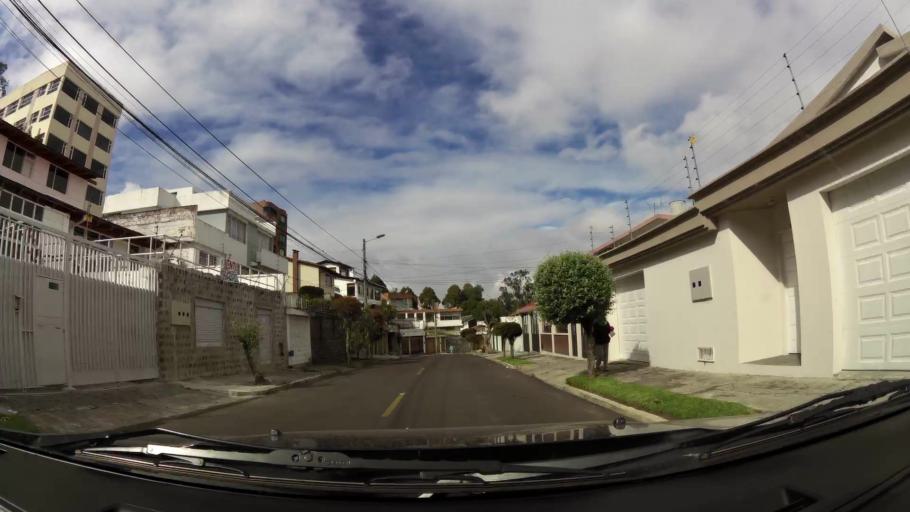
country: EC
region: Pichincha
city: Quito
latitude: -0.1809
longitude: -78.4736
